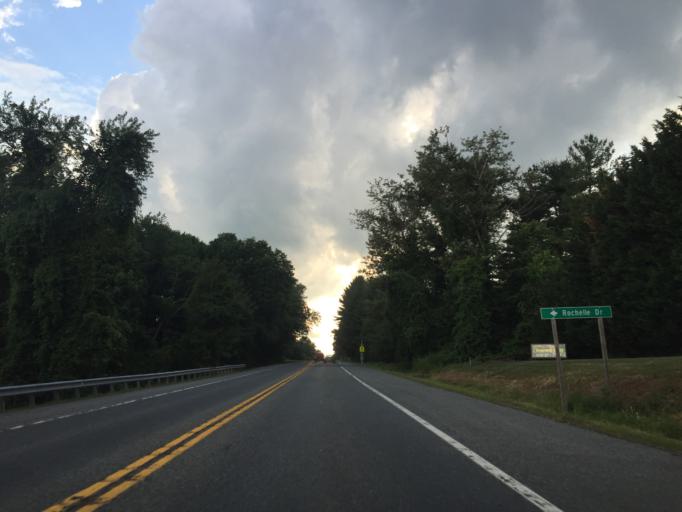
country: US
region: Maryland
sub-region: Harford County
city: Fallston
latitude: 39.5213
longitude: -76.4188
